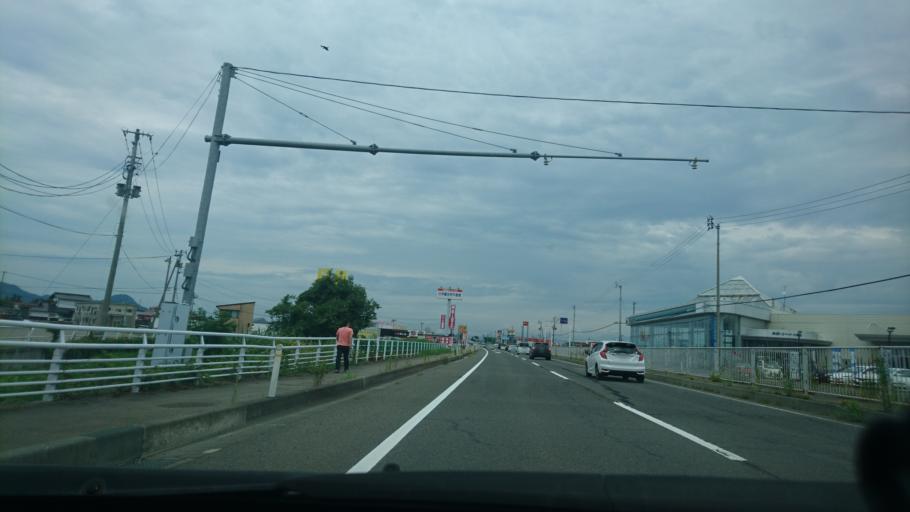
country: JP
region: Akita
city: Omagari
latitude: 39.4546
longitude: 140.4983
